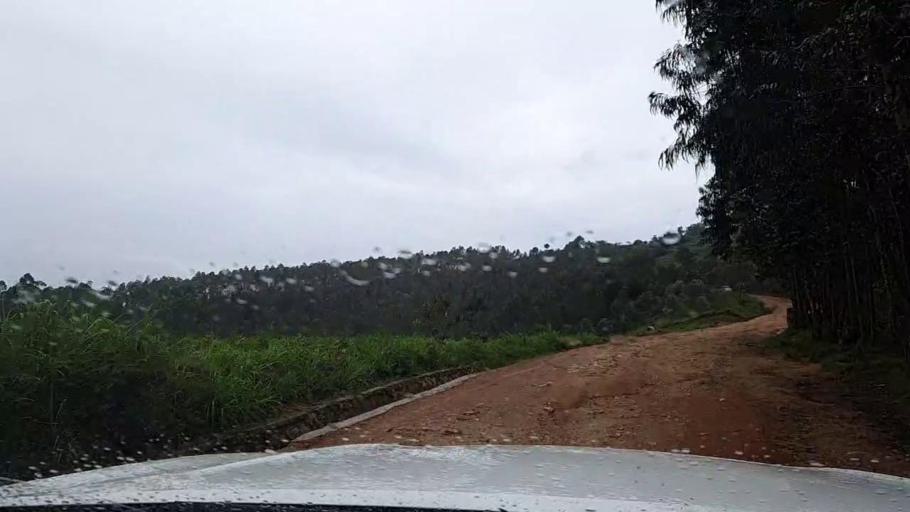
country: RW
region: Southern Province
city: Nzega
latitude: -2.4679
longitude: 29.5017
